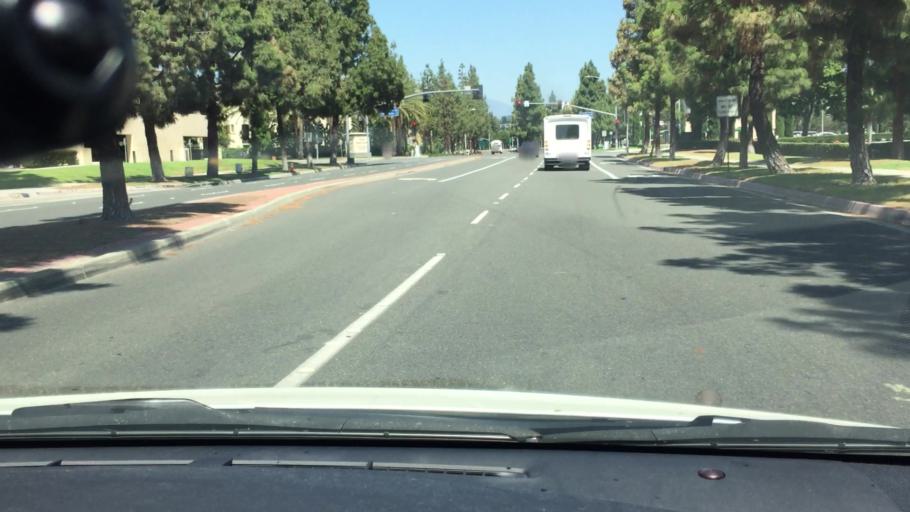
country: US
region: California
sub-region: Orange County
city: Santa Ana
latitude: 33.6901
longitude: -117.8791
